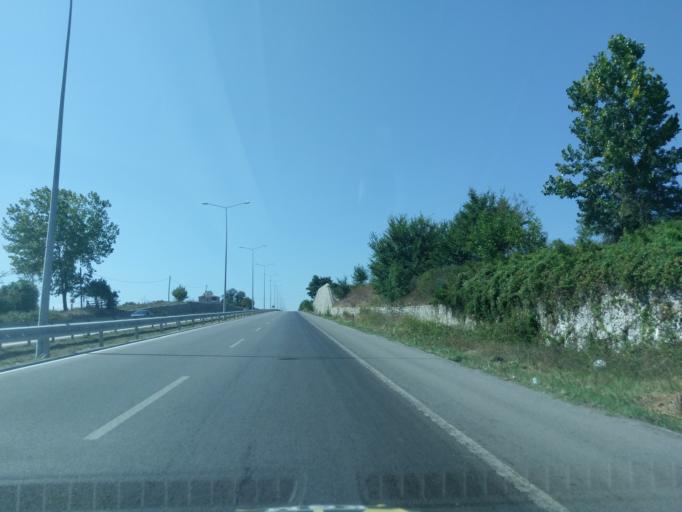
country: TR
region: Samsun
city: Bafra
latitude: 41.5228
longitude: 35.9829
